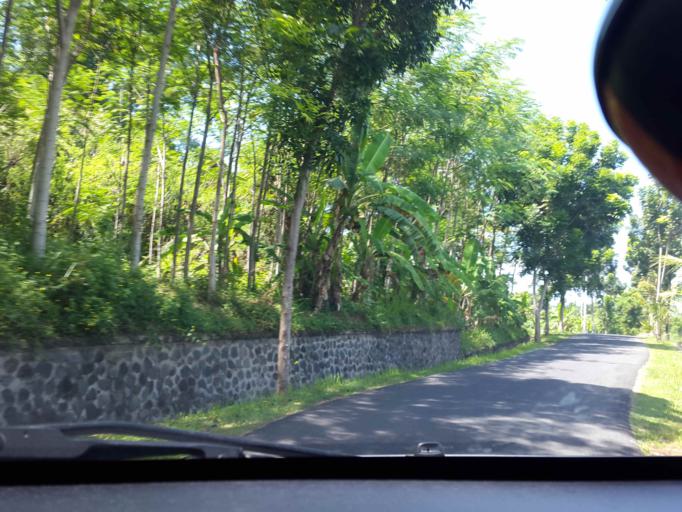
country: ID
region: Bali
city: Klungkung
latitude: -8.5349
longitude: 115.3926
